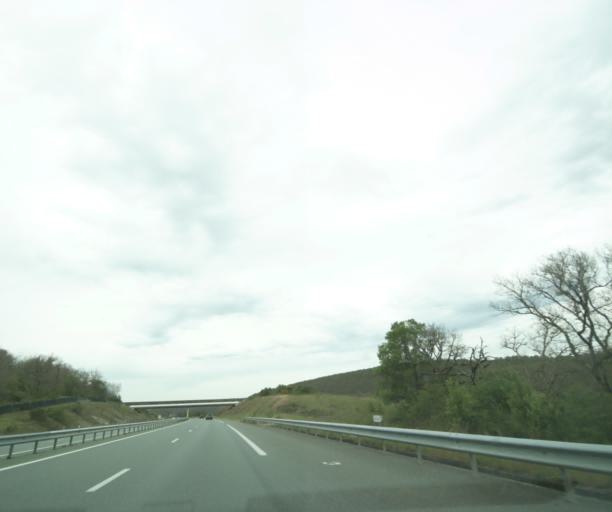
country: FR
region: Midi-Pyrenees
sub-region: Departement du Lot
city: Le Vigan
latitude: 44.7722
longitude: 1.5382
